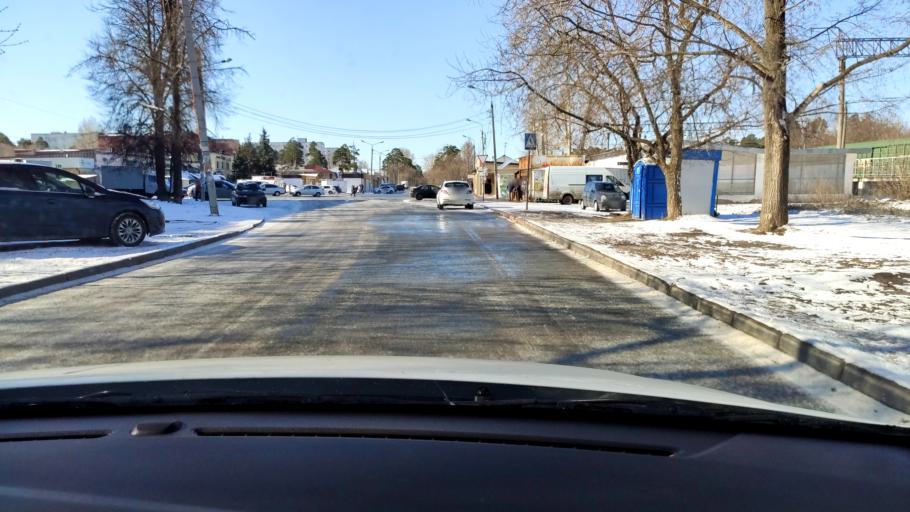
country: RU
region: Tatarstan
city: Vysokaya Gora
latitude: 55.8728
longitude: 49.2237
